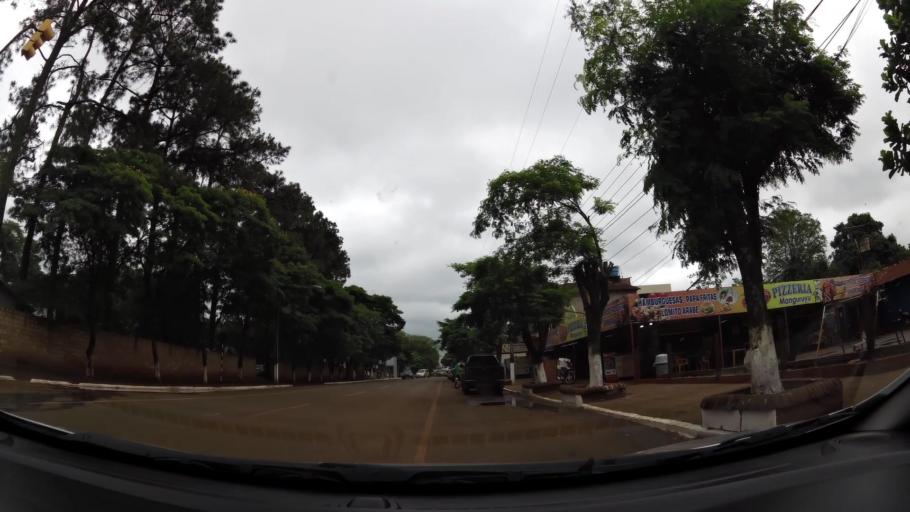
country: PY
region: Alto Parana
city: Ciudad del Este
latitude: -25.4857
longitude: -54.7596
